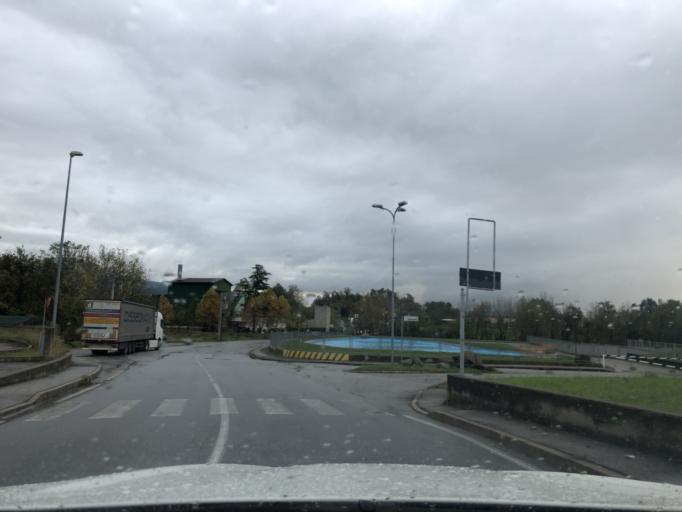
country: IT
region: Lombardy
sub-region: Provincia di Lecco
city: Suello
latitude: 45.8137
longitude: 9.3102
